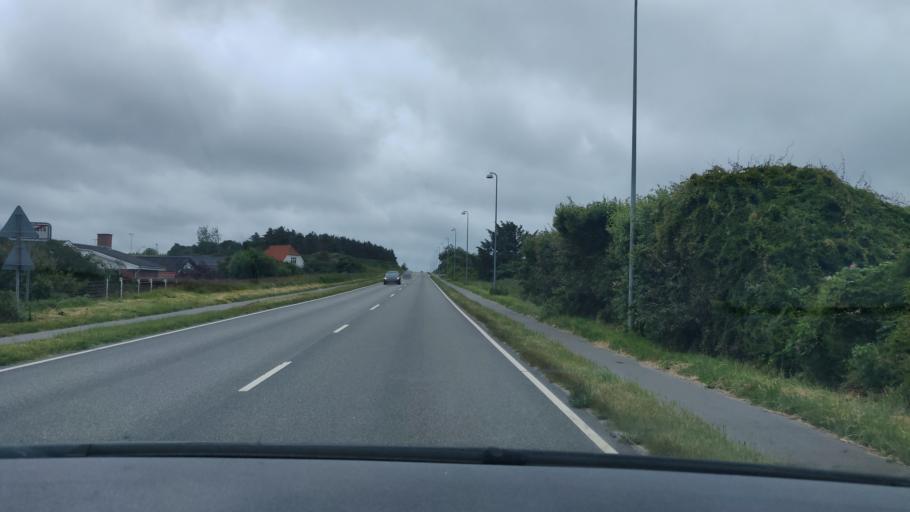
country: DK
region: North Denmark
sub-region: Hjorring Kommune
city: Hirtshals
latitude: 57.5870
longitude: 9.9568
